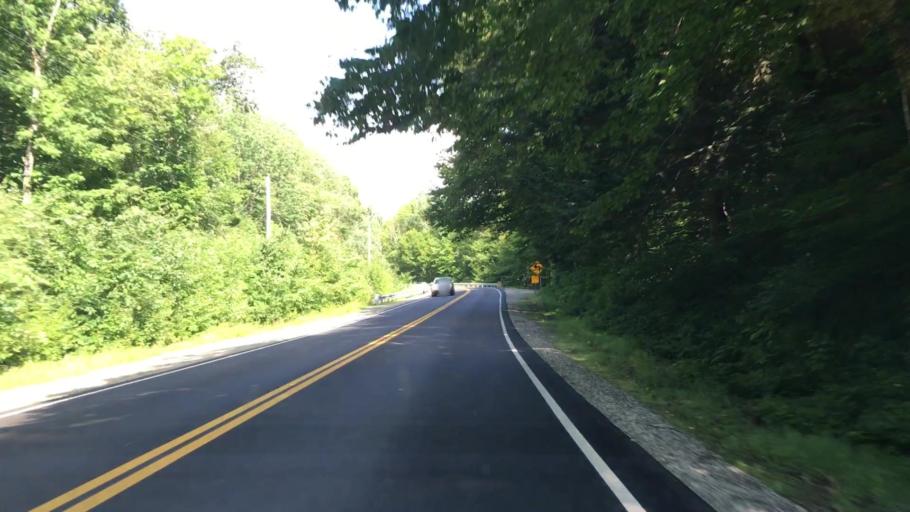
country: US
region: New Hampshire
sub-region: Grafton County
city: North Haverhill
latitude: 44.1055
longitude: -71.8785
